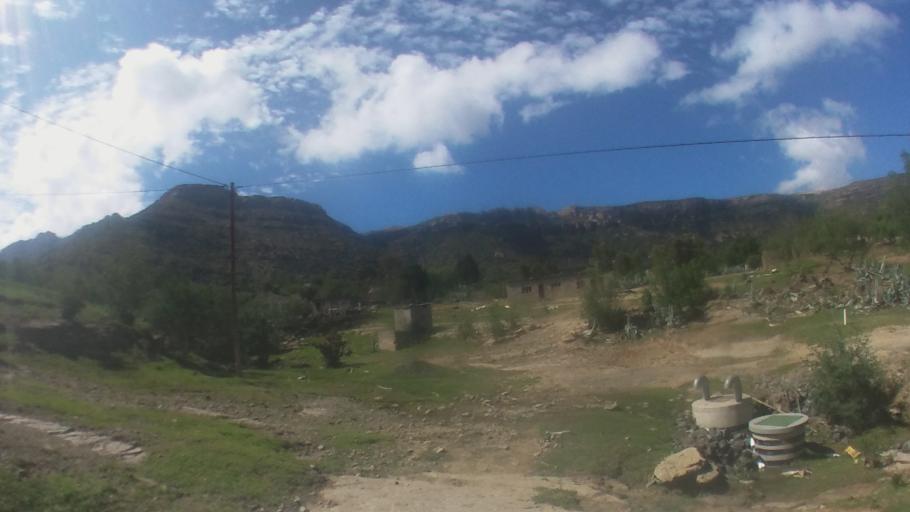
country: LS
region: Maseru
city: Nako
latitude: -29.6267
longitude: 27.5127
